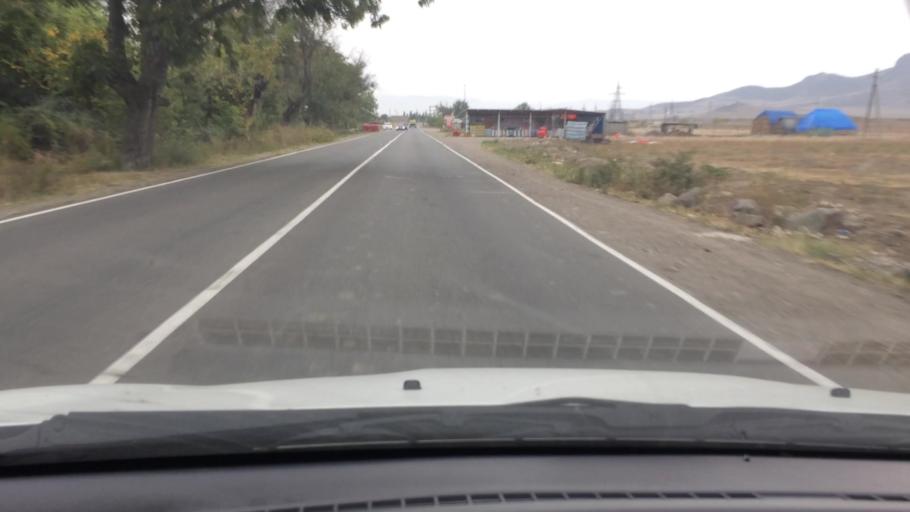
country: GE
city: Naghvarevi
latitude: 41.3974
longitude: 44.8257
